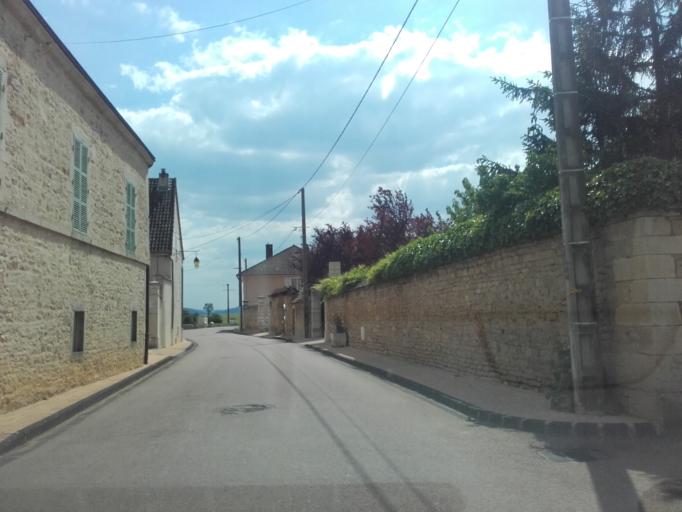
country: FR
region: Bourgogne
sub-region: Departement de la Cote-d'Or
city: Meursault
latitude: 46.9710
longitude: 4.7677
